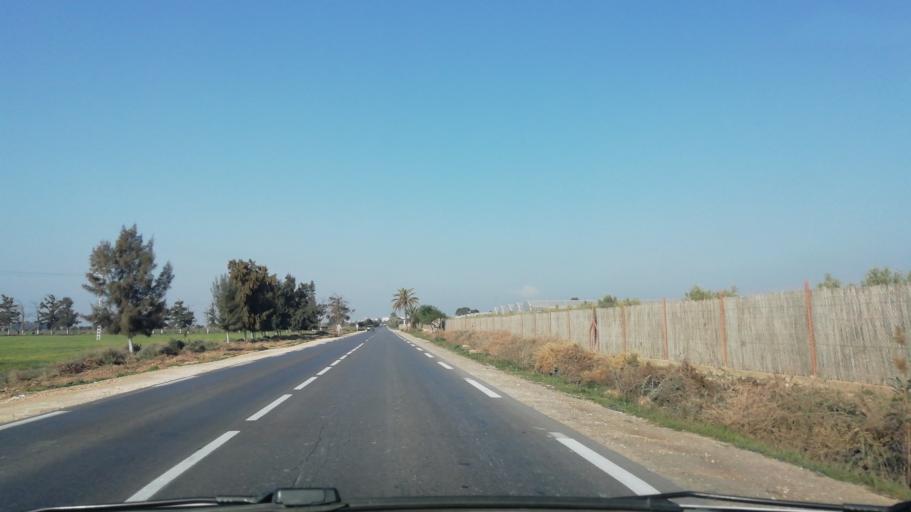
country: DZ
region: Mostaganem
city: Mostaganem
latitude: 35.7415
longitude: 0.0026
